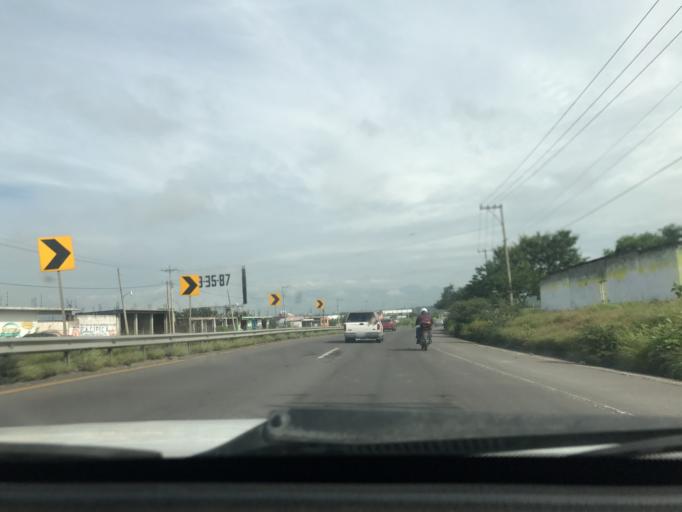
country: MX
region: Morelos
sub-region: Yecapixtla
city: Juan Morales
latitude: 18.8235
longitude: -98.9218
